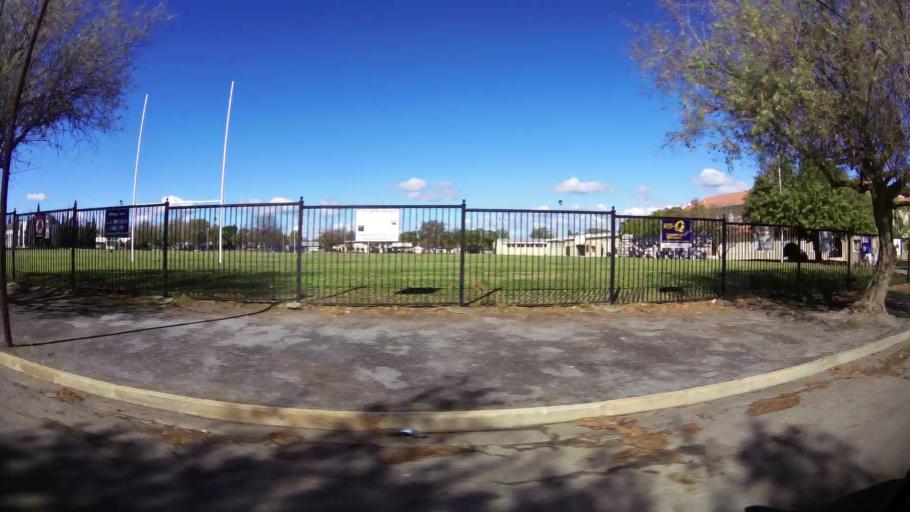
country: ZA
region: Western Cape
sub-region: Cape Winelands District Municipality
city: Ashton
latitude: -33.8051
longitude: 19.8897
